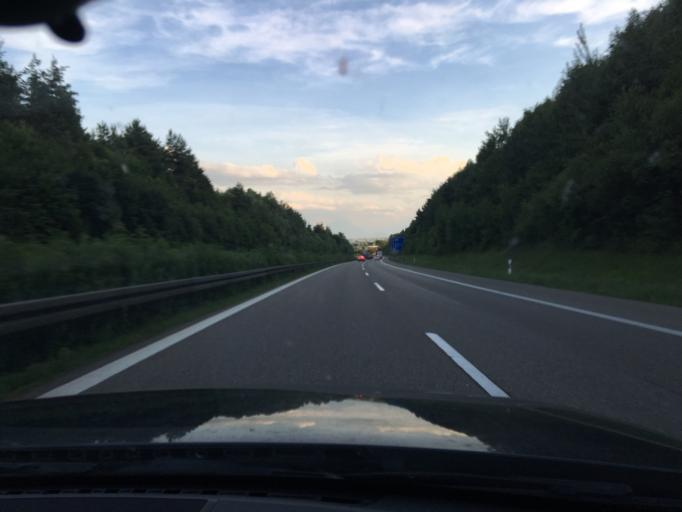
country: AT
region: Vorarlberg
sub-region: Politischer Bezirk Bregenz
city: Horbranz
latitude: 47.5602
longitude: 9.7368
